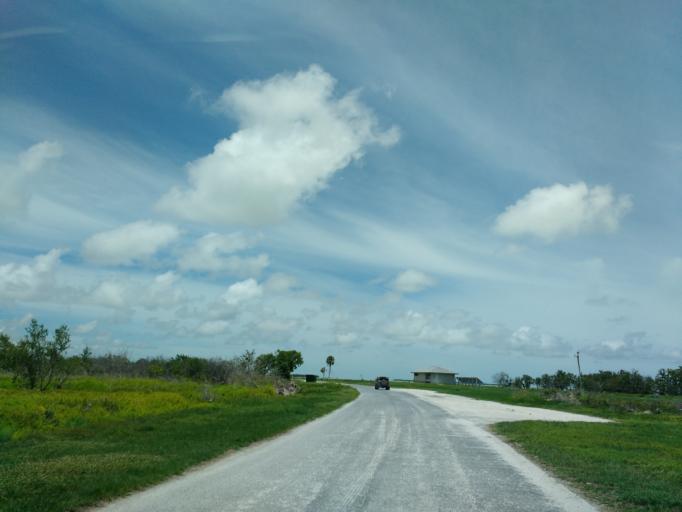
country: US
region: Florida
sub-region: Monroe County
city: Islamorada
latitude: 25.1376
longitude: -80.9380
